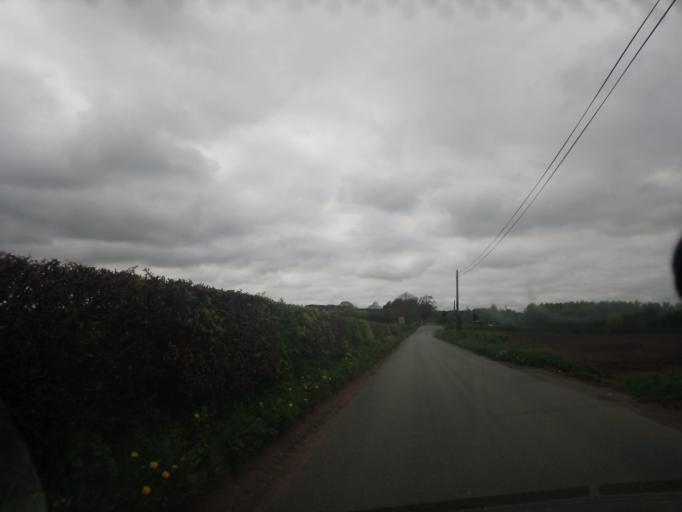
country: GB
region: England
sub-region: Shropshire
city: Stoke upon Tern
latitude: 52.8480
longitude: -2.5549
